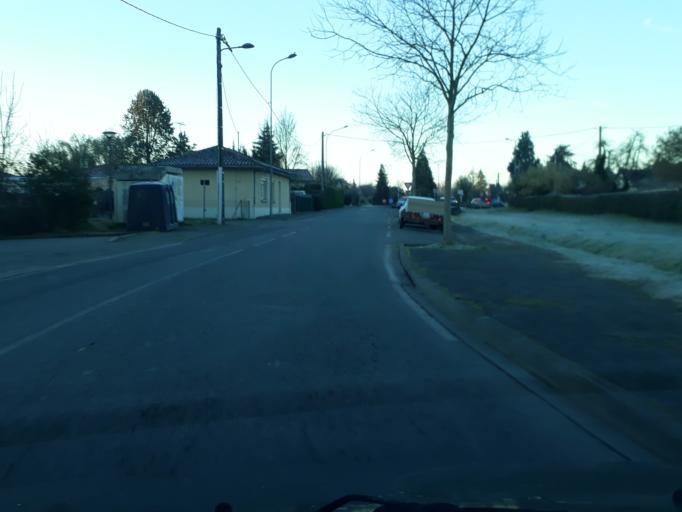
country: FR
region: Midi-Pyrenees
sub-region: Departement du Gers
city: Auch
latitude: 43.6309
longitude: 0.5879
